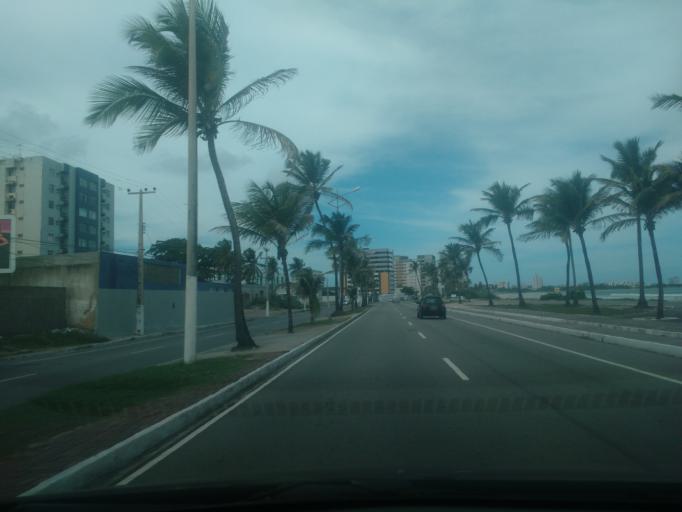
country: BR
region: Alagoas
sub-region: Maceio
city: Maceio
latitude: -9.6714
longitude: -35.7438
